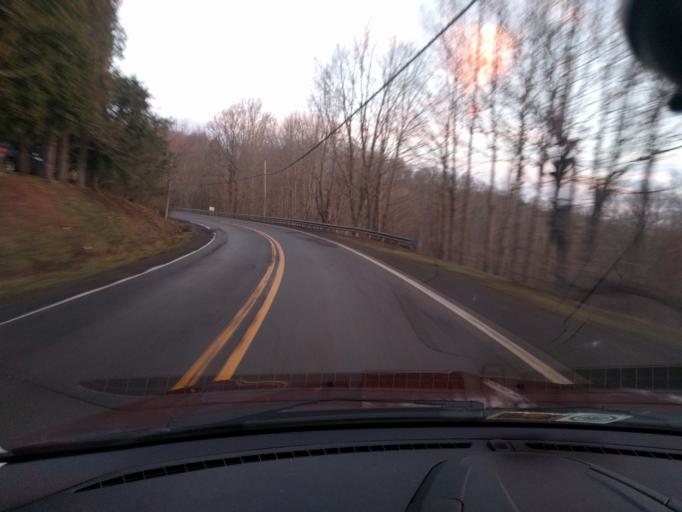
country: US
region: West Virginia
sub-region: Greenbrier County
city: Rainelle
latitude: 38.0070
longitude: -80.8785
